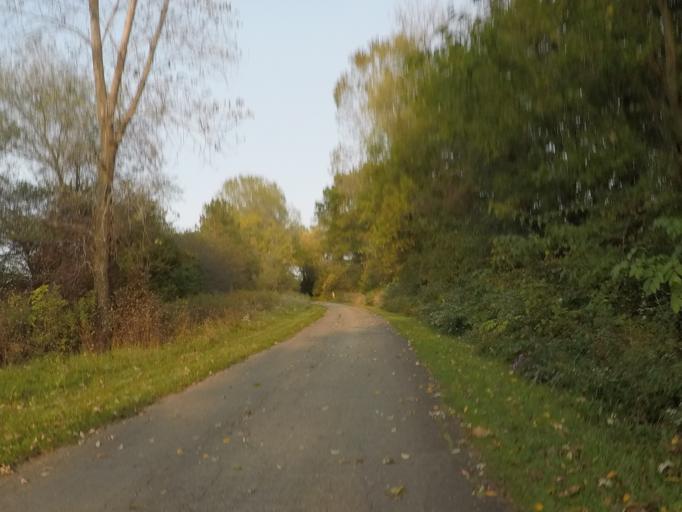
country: US
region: Wisconsin
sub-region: Dane County
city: Verona
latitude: 42.9930
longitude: -89.5073
